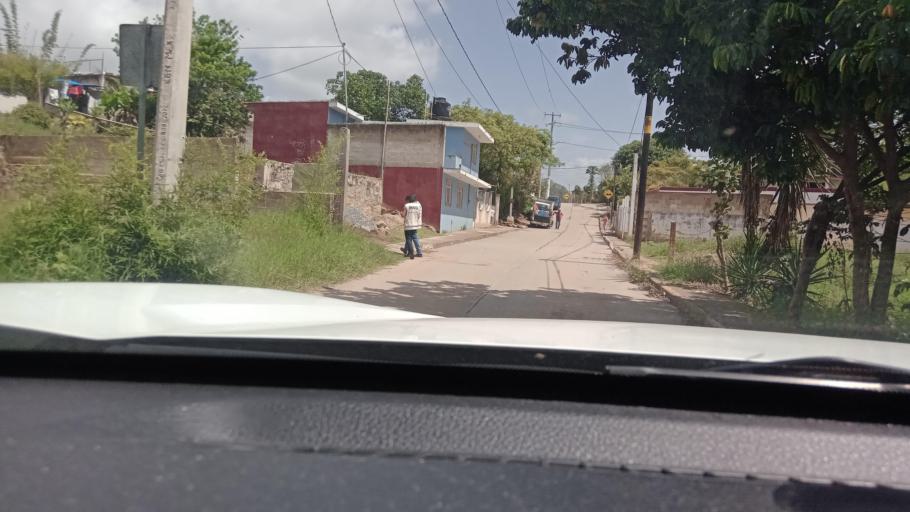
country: MX
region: Veracruz
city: El Castillo
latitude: 19.5642
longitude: -96.8605
